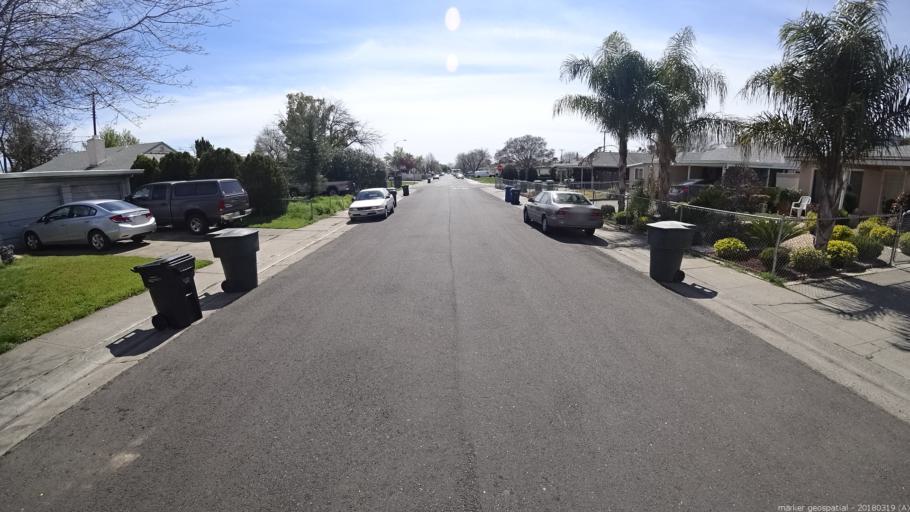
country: US
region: California
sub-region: Sacramento County
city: Parkway
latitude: 38.5138
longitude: -121.4528
